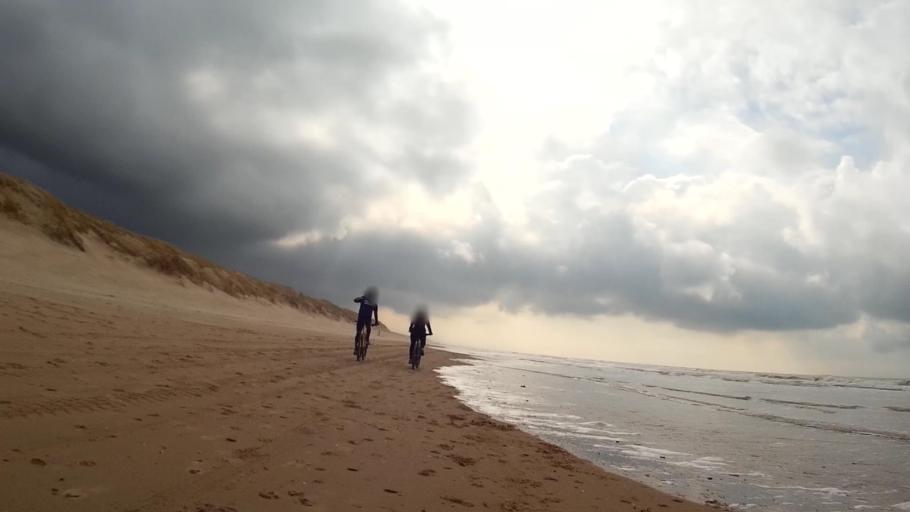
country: NL
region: North Holland
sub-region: Gemeente Bergen
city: Egmond aan Zee
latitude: 52.6959
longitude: 4.6349
